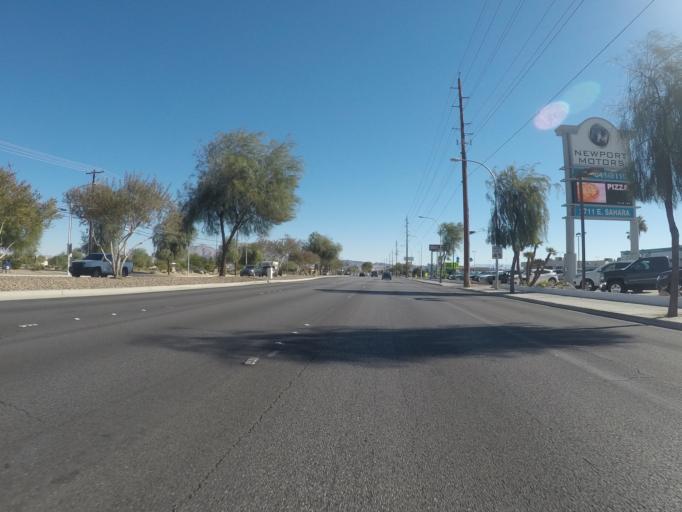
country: US
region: Nevada
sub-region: Clark County
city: Winchester
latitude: 36.1443
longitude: -115.1139
